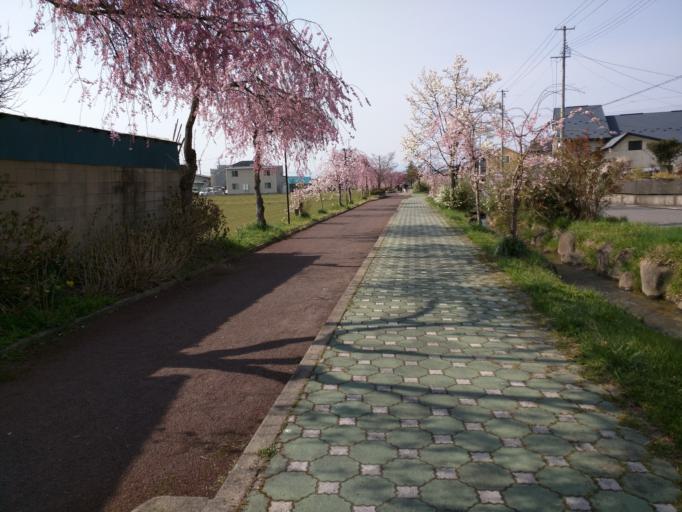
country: JP
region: Fukushima
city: Kitakata
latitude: 37.6502
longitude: 139.8636
